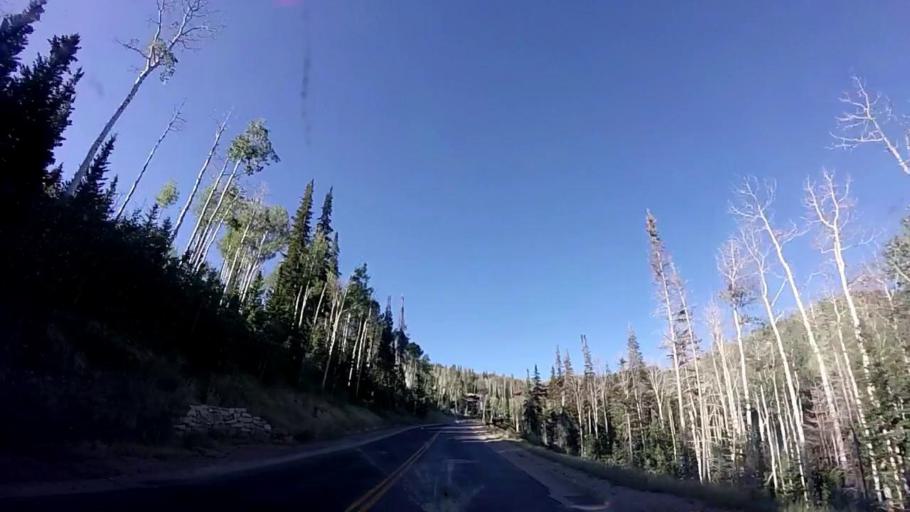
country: US
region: Utah
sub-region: Summit County
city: Park City
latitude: 40.6229
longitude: -111.5021
